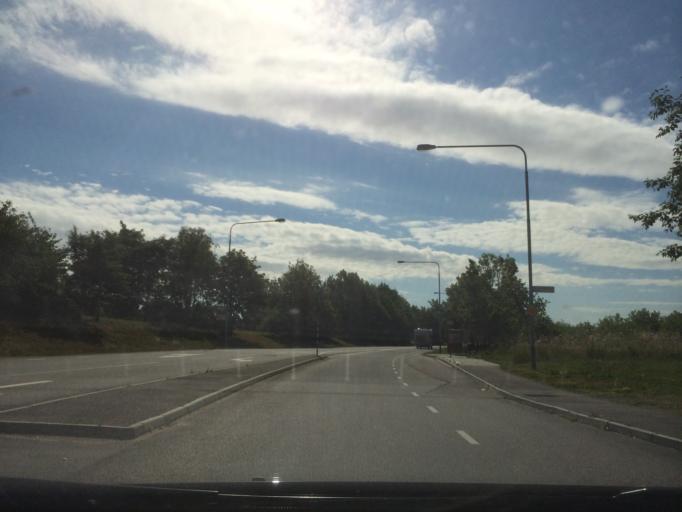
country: SE
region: Skane
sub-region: Malmo
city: Bunkeflostrand
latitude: 55.5729
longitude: 12.9362
